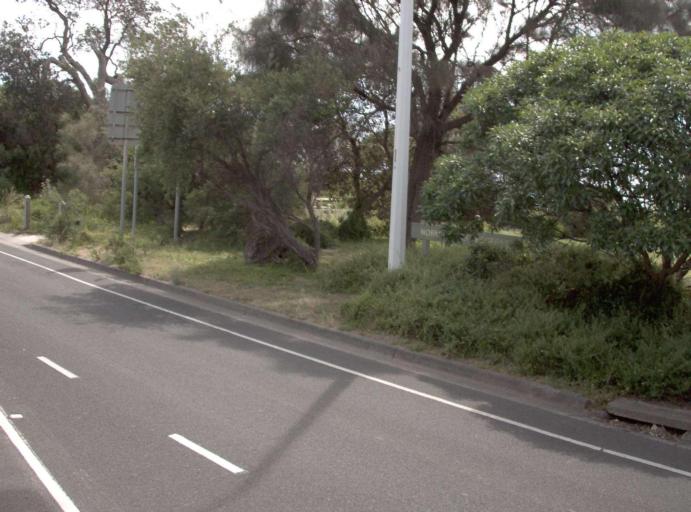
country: AU
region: Victoria
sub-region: Mornington Peninsula
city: Dromana
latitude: -38.3335
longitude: 144.9632
